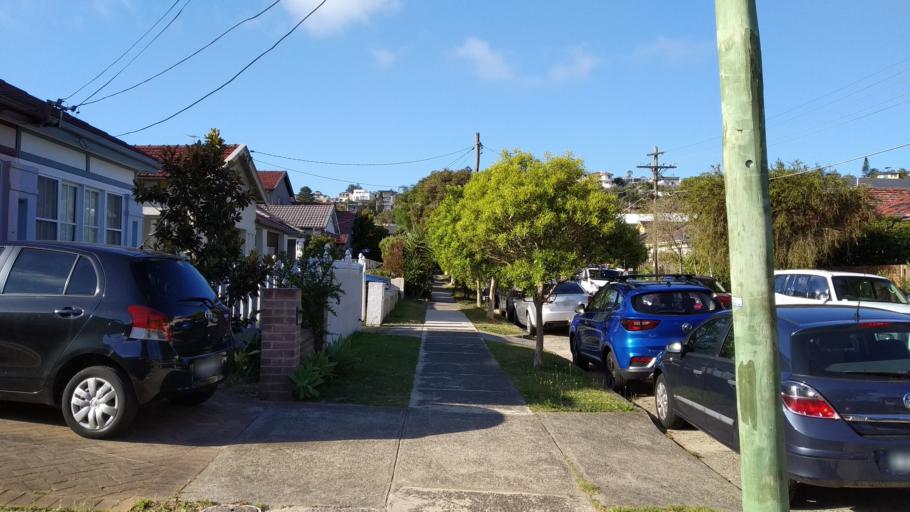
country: AU
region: New South Wales
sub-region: Waverley
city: North Bondi
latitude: -33.8839
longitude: 151.2789
